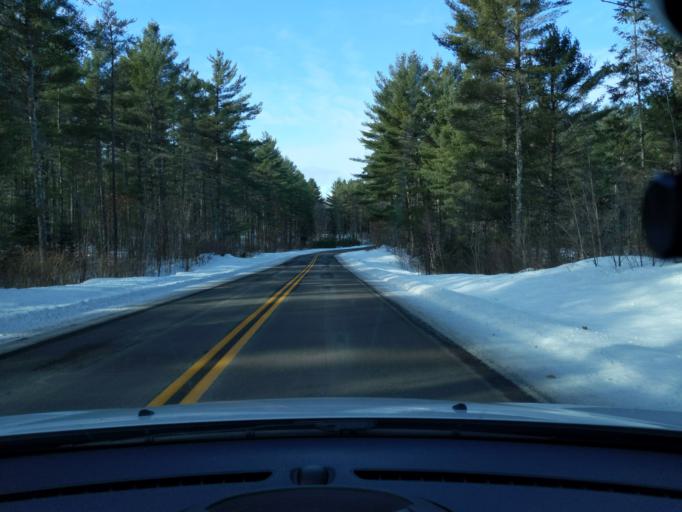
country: US
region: Wisconsin
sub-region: Sawyer County
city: Little Round Lake
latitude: 46.1116
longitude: -91.3130
